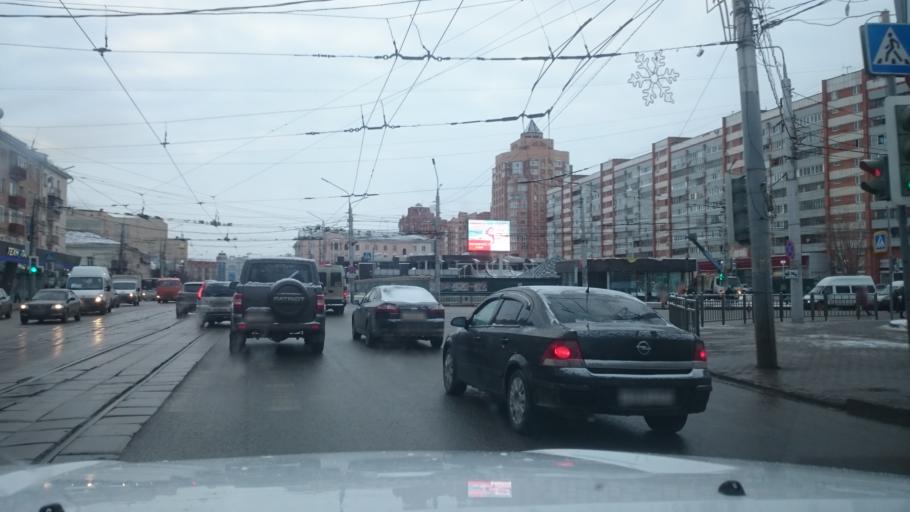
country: RU
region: Tula
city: Tula
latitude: 54.1966
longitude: 37.6118
